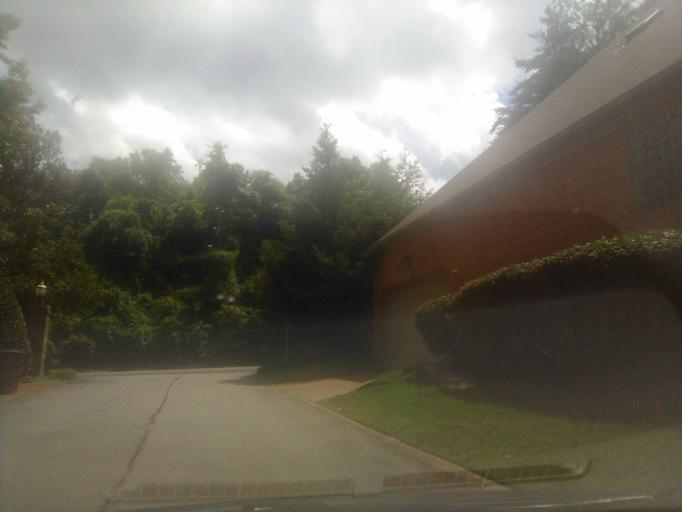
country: US
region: Tennessee
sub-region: Davidson County
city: Belle Meade
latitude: 36.1098
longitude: -86.8363
